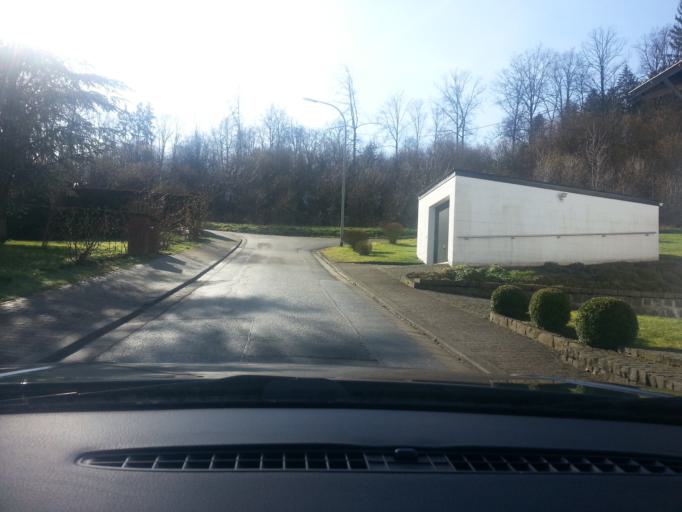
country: DE
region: Rheinland-Pfalz
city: Herchweiler
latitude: 49.5107
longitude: 7.2684
